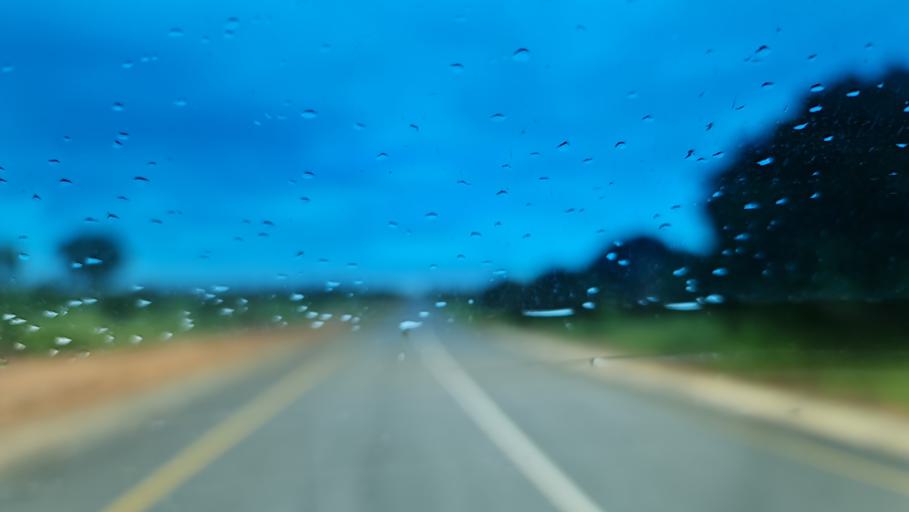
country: MZ
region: Nampula
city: Nampula
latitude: -15.5362
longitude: 39.3302
